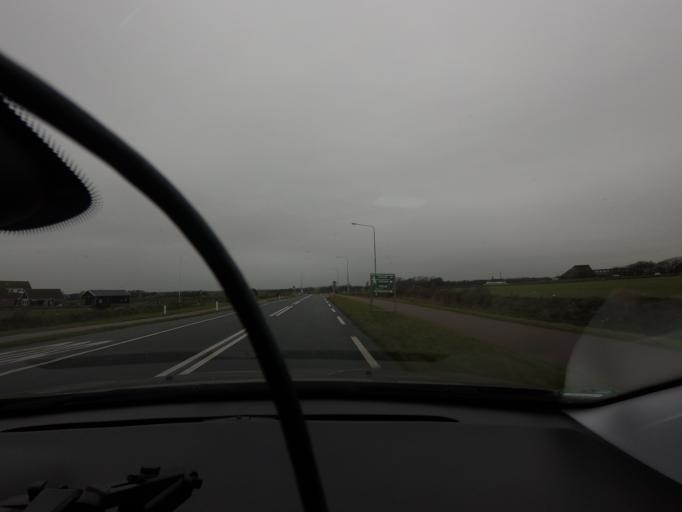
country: NL
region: North Holland
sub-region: Gemeente Texel
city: Den Burg
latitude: 53.0424
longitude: 4.7998
